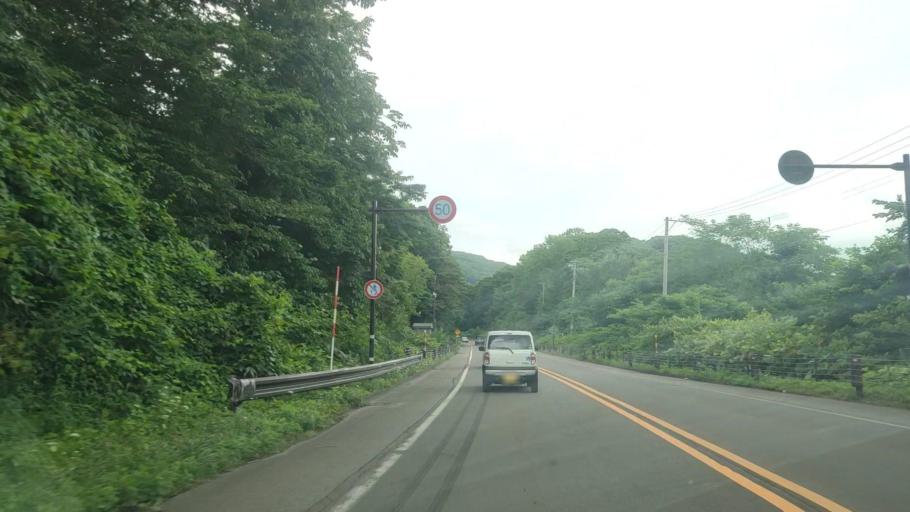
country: JP
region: Hokkaido
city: Nanae
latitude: 41.9704
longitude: 140.6510
